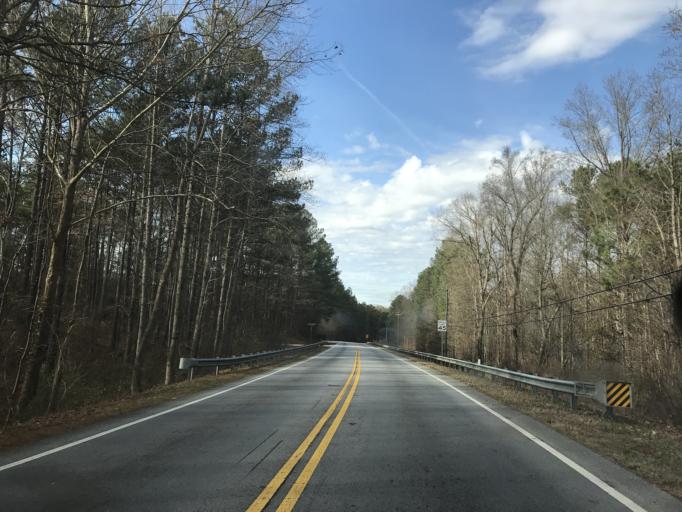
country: US
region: Georgia
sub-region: Douglas County
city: Douglasville
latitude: 33.7896
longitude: -84.8000
